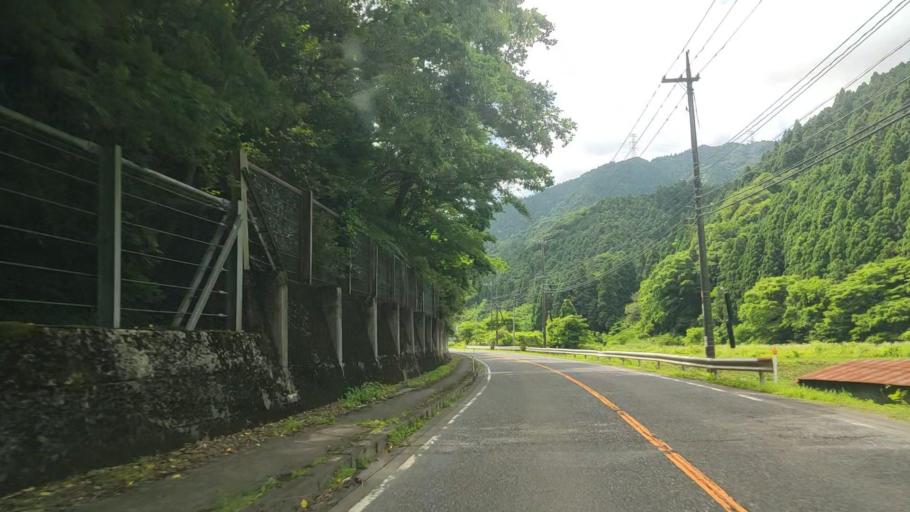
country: JP
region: Okayama
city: Niimi
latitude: 35.2194
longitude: 133.4528
